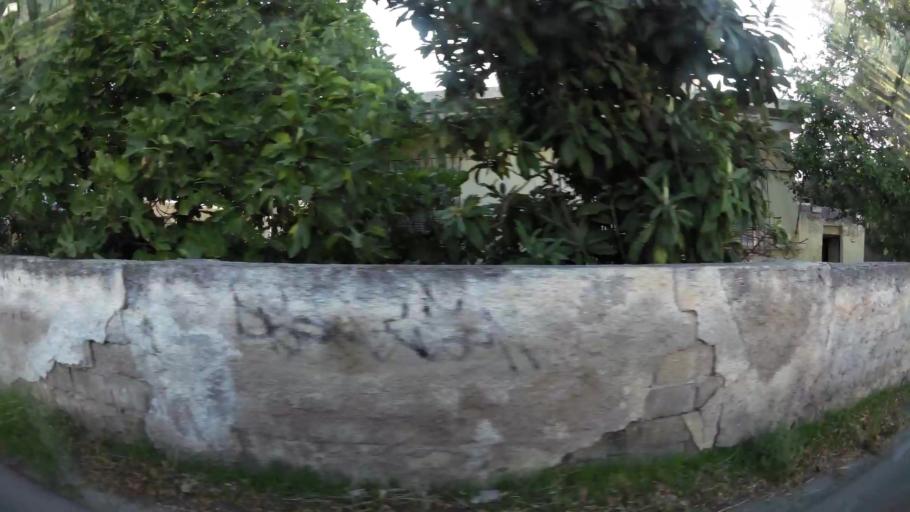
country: GR
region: Attica
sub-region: Nomarchia Athinas
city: Nea Filadelfeia
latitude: 38.0497
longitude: 23.7318
